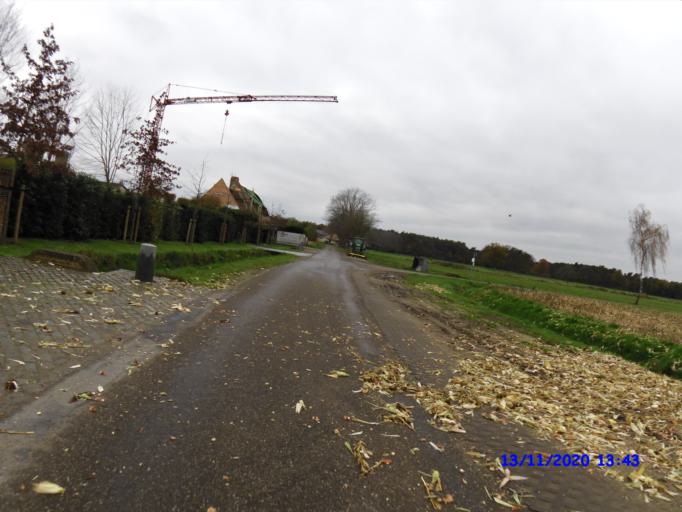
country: BE
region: Flanders
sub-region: Provincie Antwerpen
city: Kasterlee
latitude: 51.2576
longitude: 4.9863
